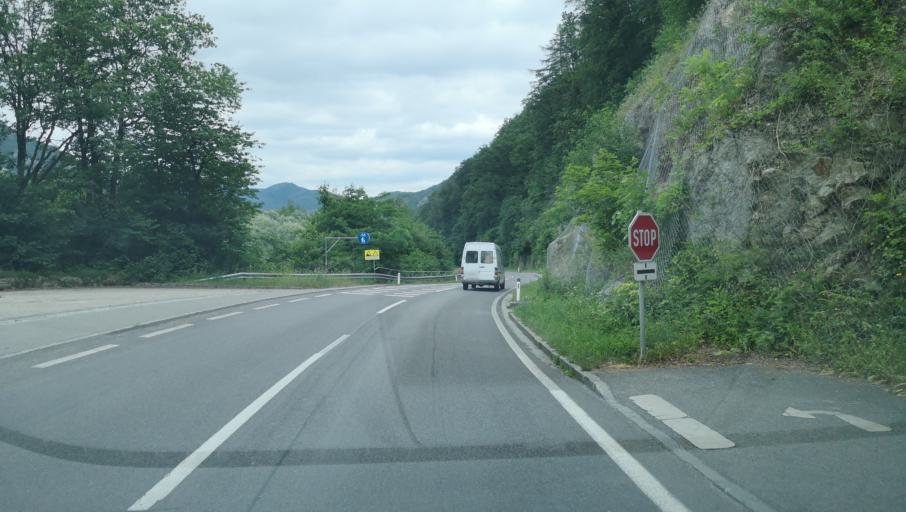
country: AT
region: Lower Austria
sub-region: Politischer Bezirk Krems
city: Aggsbach
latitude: 48.2697
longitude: 15.3847
